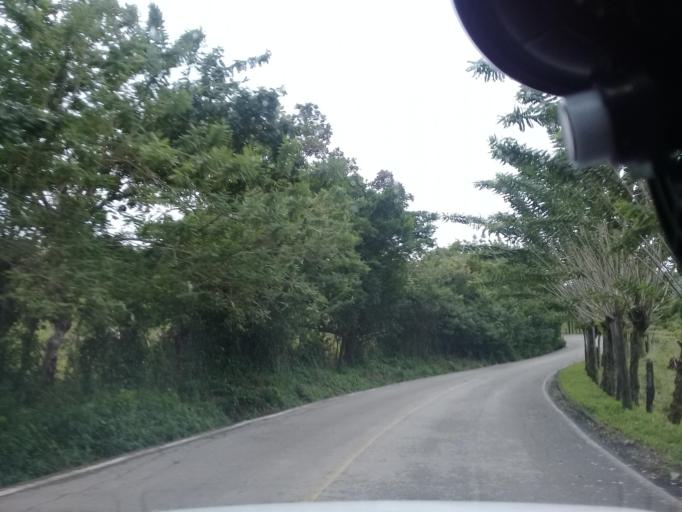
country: MX
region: Veracruz
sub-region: Chalma
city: San Pedro Coyutla
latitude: 21.2144
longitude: -98.4258
